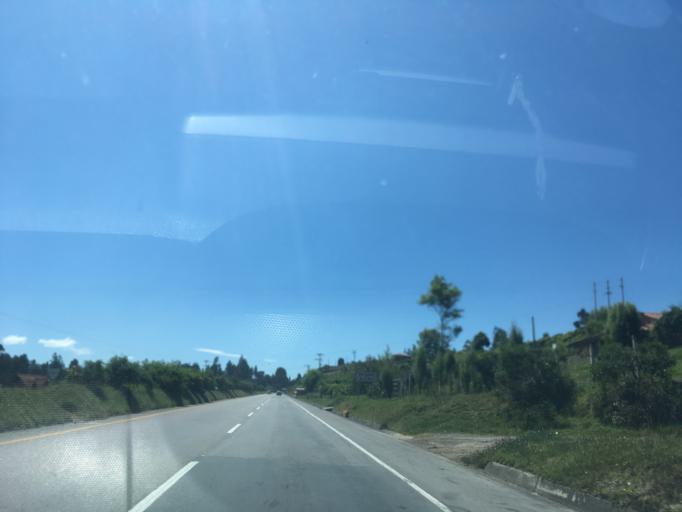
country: CO
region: Boyaca
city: Tuta
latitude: 5.7034
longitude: -73.2456
